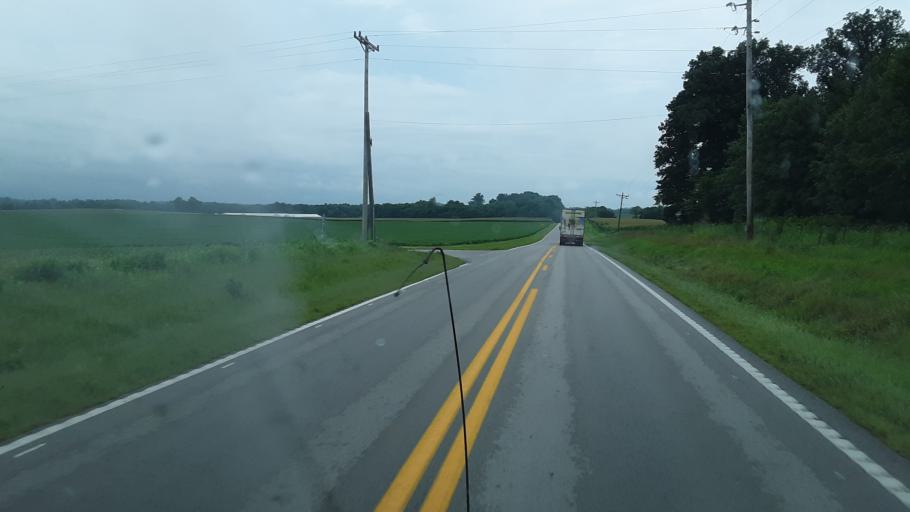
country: US
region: Kentucky
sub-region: Todd County
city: Elkton
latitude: 36.7365
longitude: -87.0683
